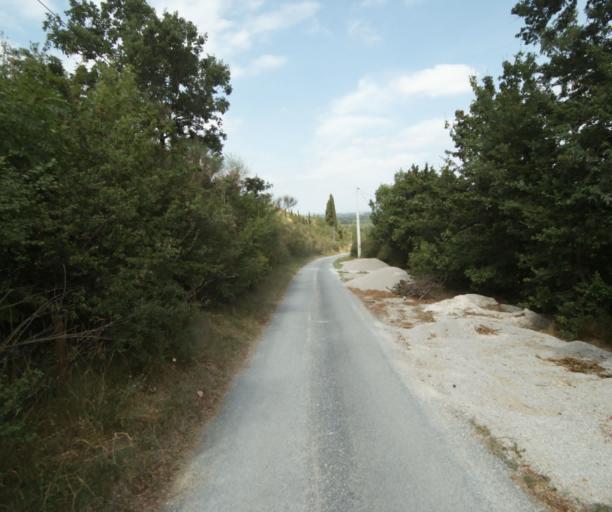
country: FR
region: Midi-Pyrenees
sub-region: Departement du Tarn
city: Soreze
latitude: 43.4447
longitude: 2.0450
